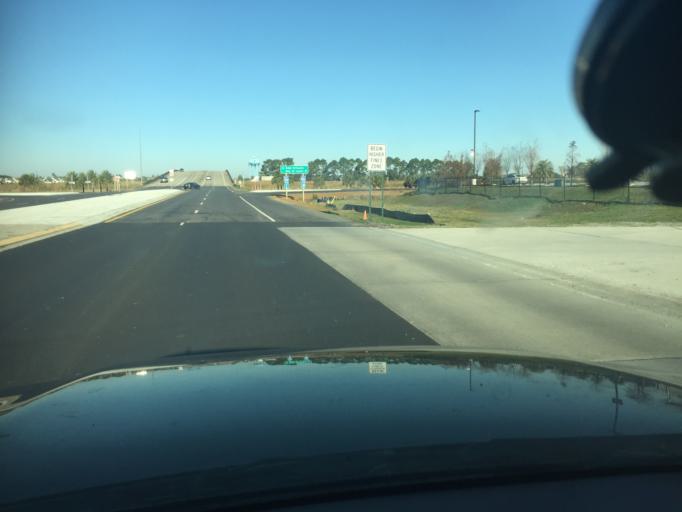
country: US
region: Louisiana
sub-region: Saint Tammany Parish
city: Eden Isle
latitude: 30.2198
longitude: -89.7803
